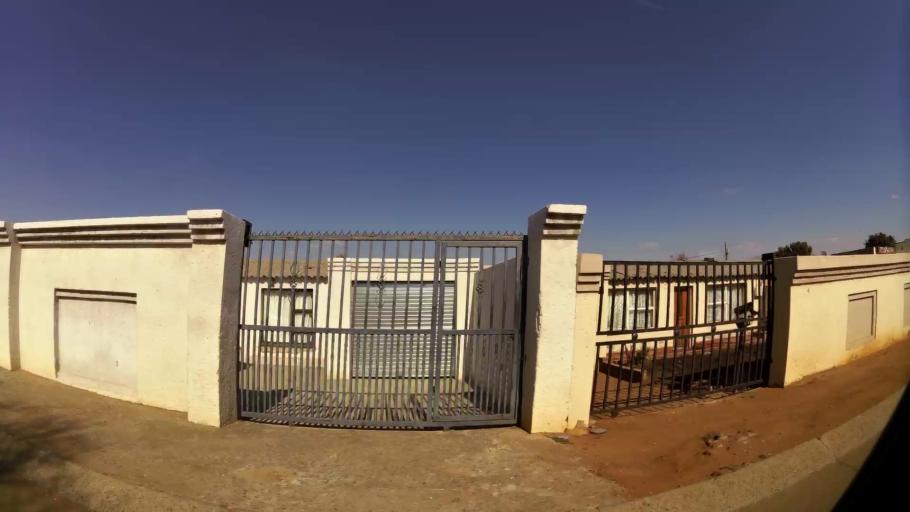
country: ZA
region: Gauteng
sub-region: City of Johannesburg Metropolitan Municipality
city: Soweto
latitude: -26.2369
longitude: 27.8794
